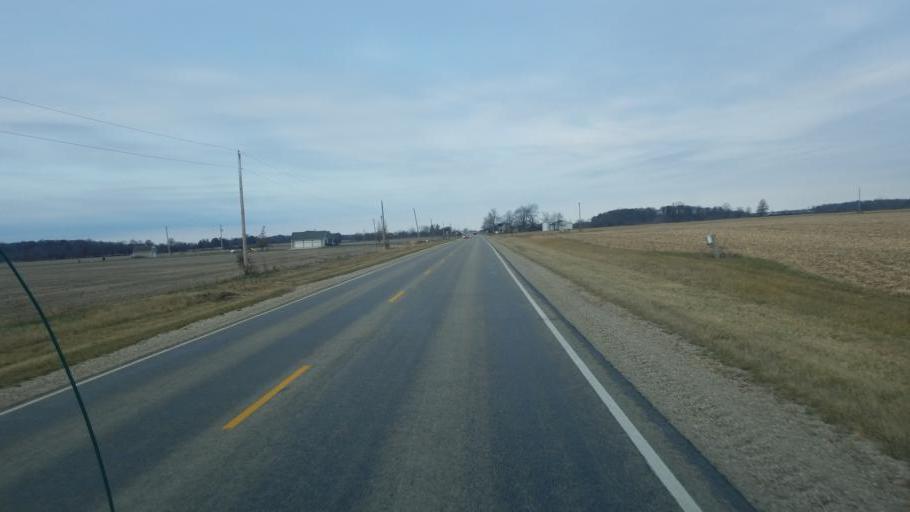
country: US
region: Indiana
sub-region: Adams County
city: Geneva
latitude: 40.5424
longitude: -84.8741
